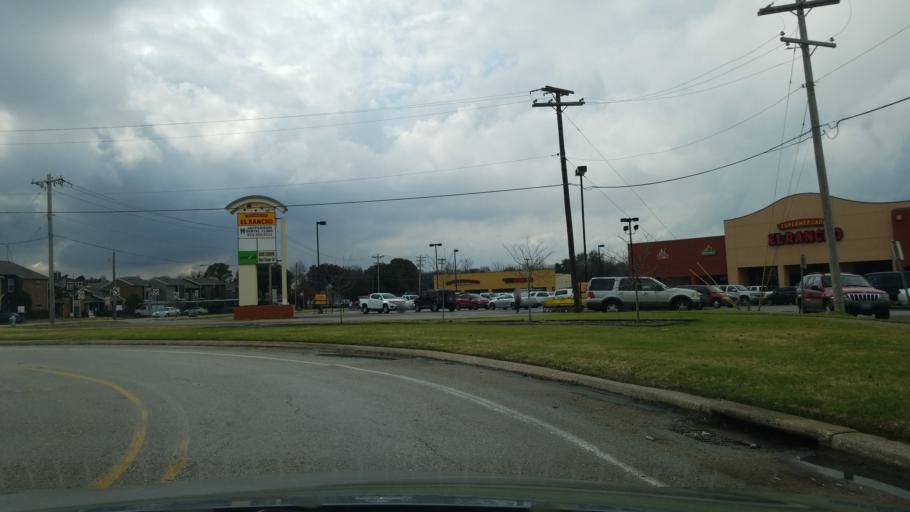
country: US
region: Texas
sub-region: Denton County
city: Lewisville
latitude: 33.0375
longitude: -97.0036
